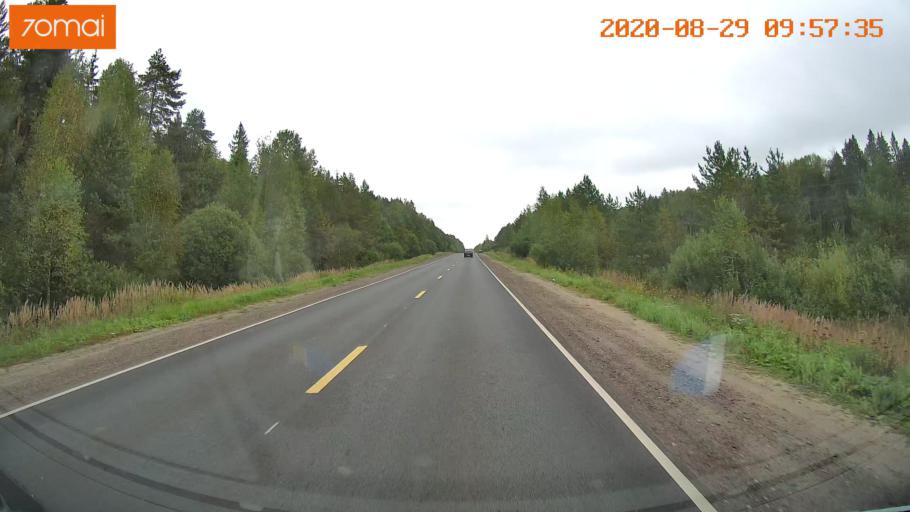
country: RU
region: Ivanovo
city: Zarechnyy
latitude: 57.4160
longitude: 42.3179
